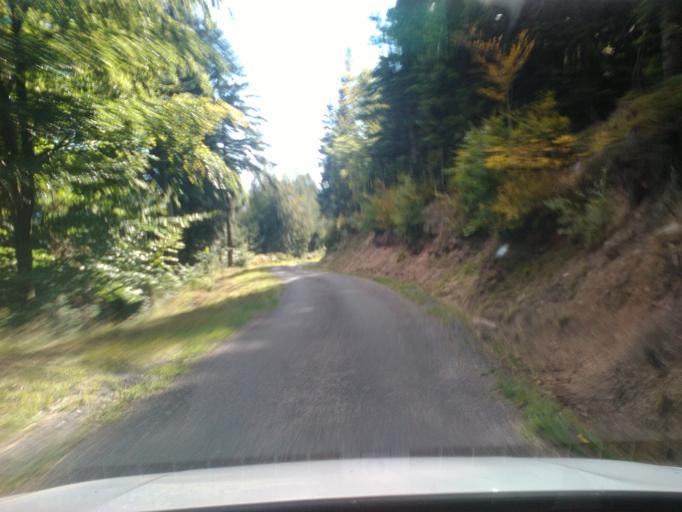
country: FR
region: Lorraine
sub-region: Departement des Vosges
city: Sainte-Marguerite
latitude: 48.3052
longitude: 7.0298
